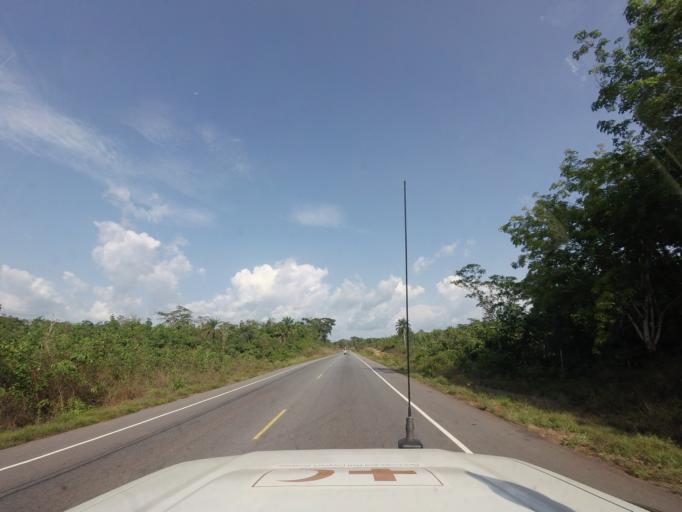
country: LR
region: Bong
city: Gbarnga
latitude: 6.8837
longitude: -9.7509
